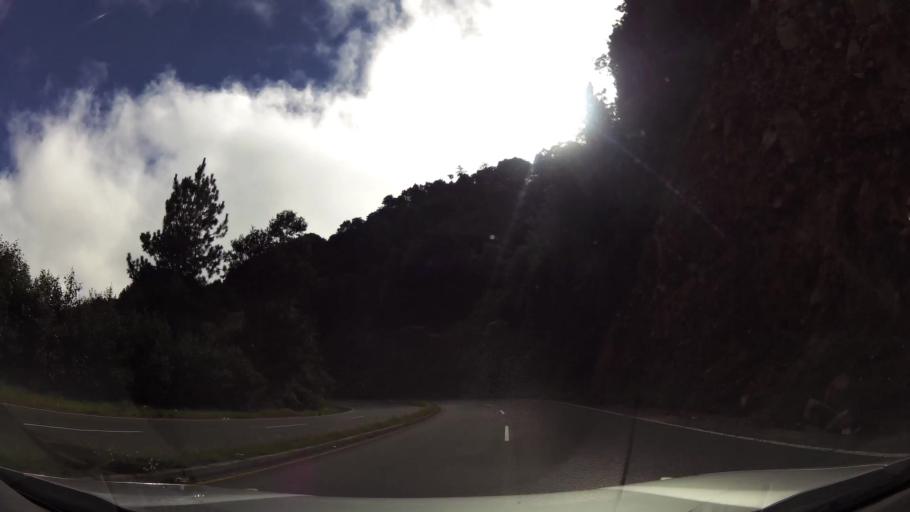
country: GT
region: Solola
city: Santa Catarina Ixtahuacan
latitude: 14.8387
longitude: -91.3927
